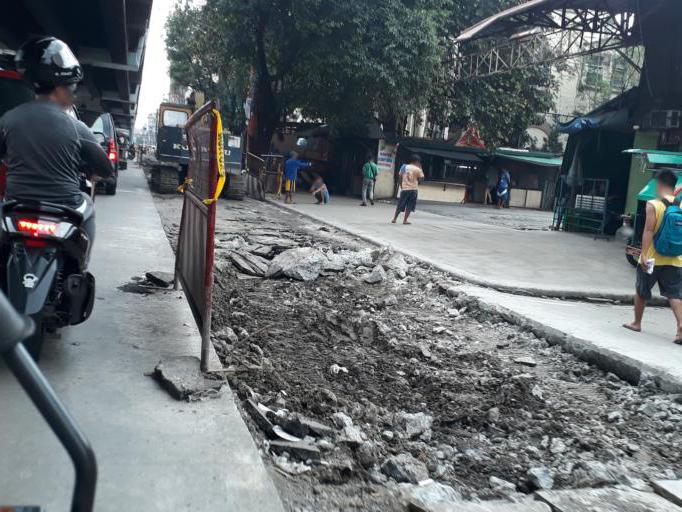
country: PH
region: Metro Manila
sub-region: City of Manila
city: Manila
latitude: 14.6055
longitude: 120.9821
